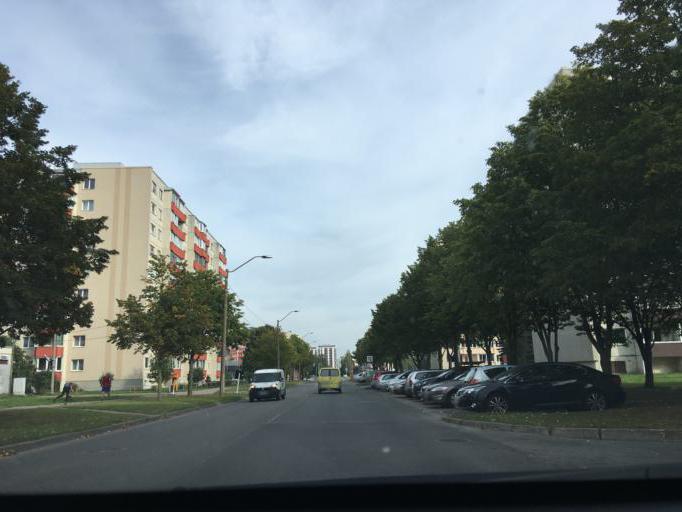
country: EE
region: Harju
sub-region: Tallinna linn
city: Kose
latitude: 59.4498
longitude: 24.8760
